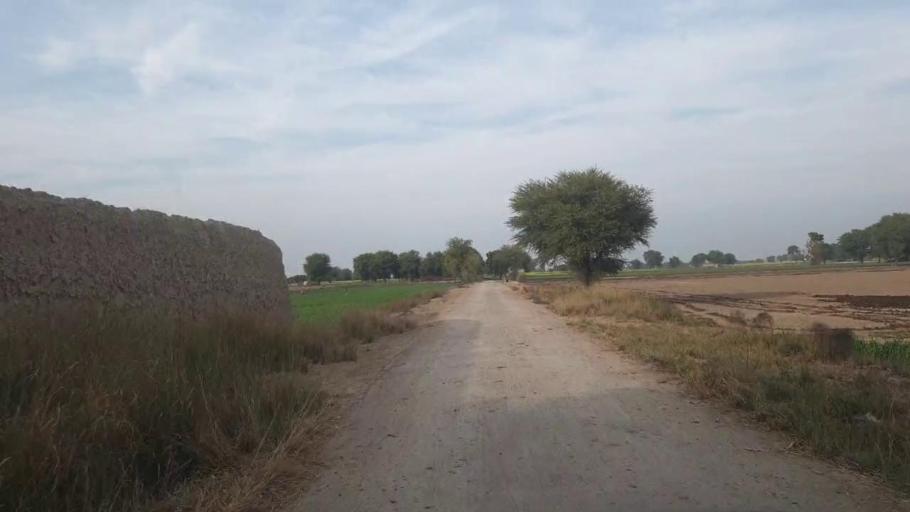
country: PK
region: Sindh
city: Shahpur Chakar
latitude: 26.1239
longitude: 68.5547
